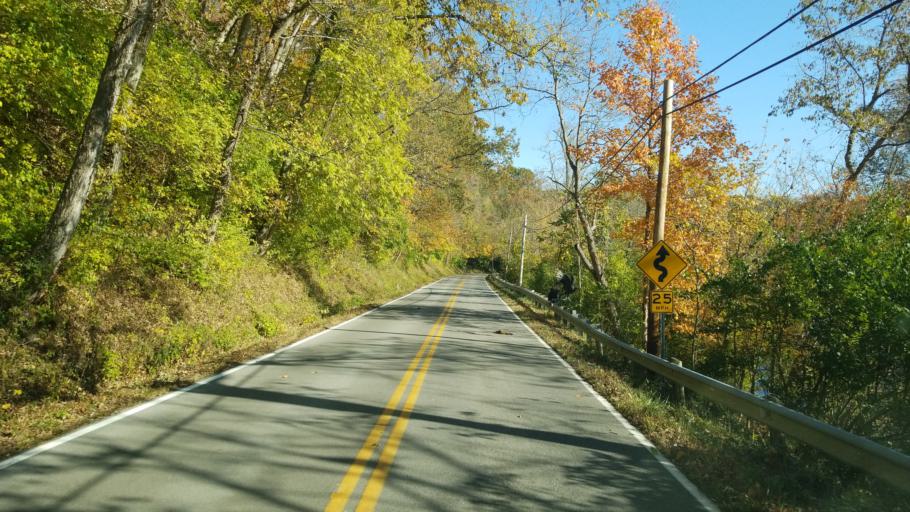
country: US
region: Ohio
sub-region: Warren County
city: Morrow
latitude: 39.3590
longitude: -84.1274
